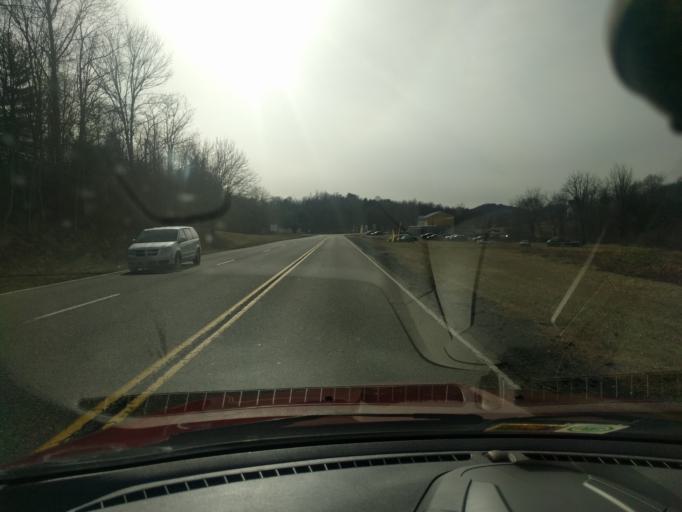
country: US
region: Virginia
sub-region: Augusta County
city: Stuarts Draft
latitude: 38.0178
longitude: -79.1415
